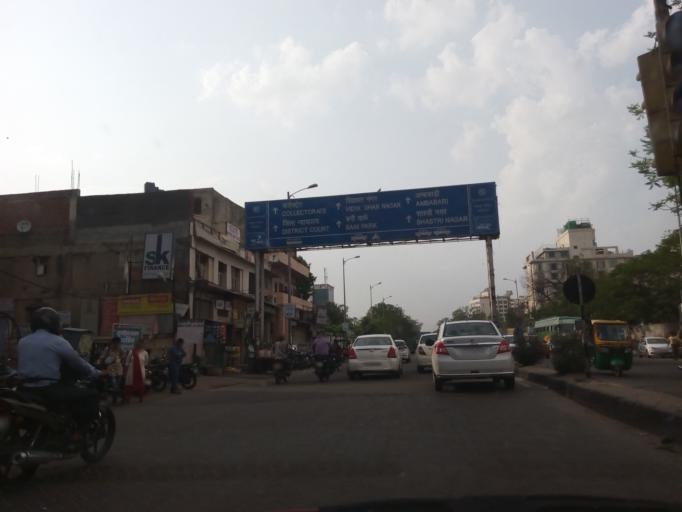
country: IN
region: Rajasthan
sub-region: Jaipur
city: Jaipur
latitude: 26.9207
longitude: 75.7940
